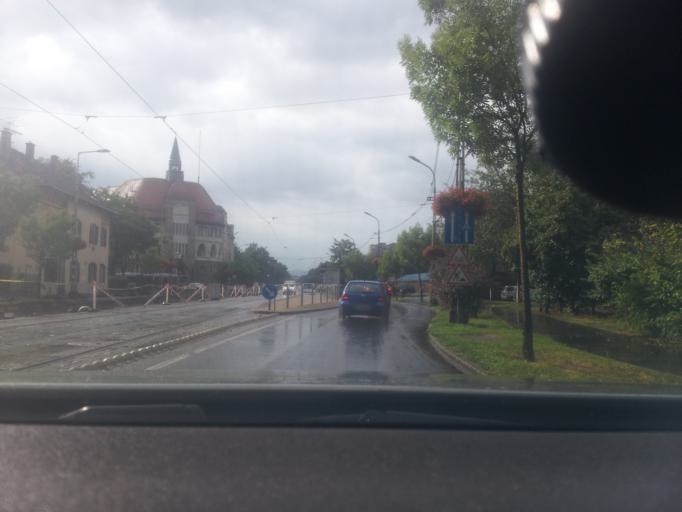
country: HU
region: Budapest
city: Budapest XIX. keruelet
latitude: 47.4556
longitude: 19.1386
